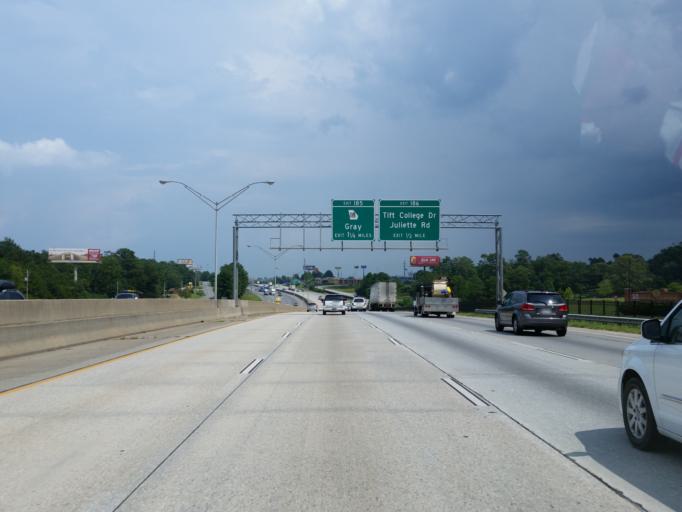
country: US
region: Georgia
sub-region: Monroe County
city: Forsyth
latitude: 33.0397
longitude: -83.9322
